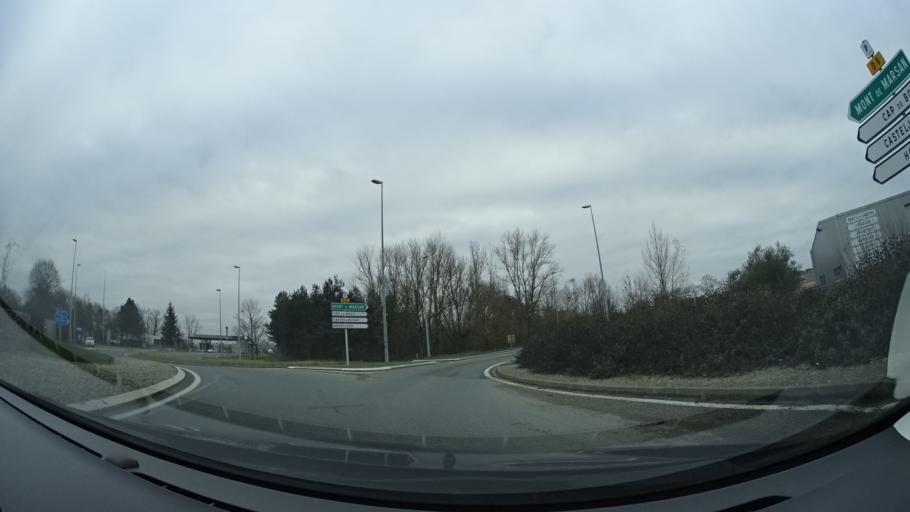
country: FR
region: Aquitaine
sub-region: Departement du Lot-et-Garonne
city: Damazan
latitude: 44.2861
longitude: 0.2694
